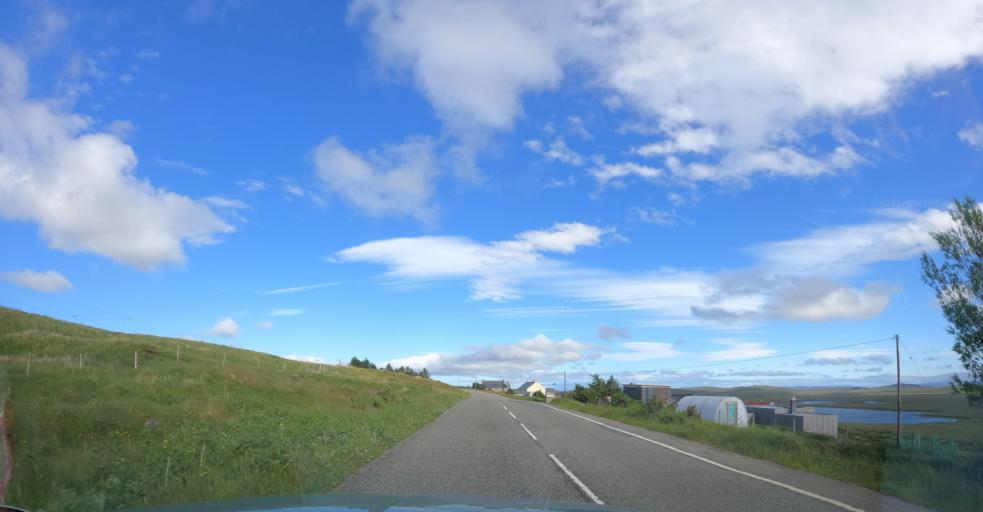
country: GB
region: Scotland
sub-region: Eilean Siar
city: Stornoway
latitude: 58.1725
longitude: -6.5893
